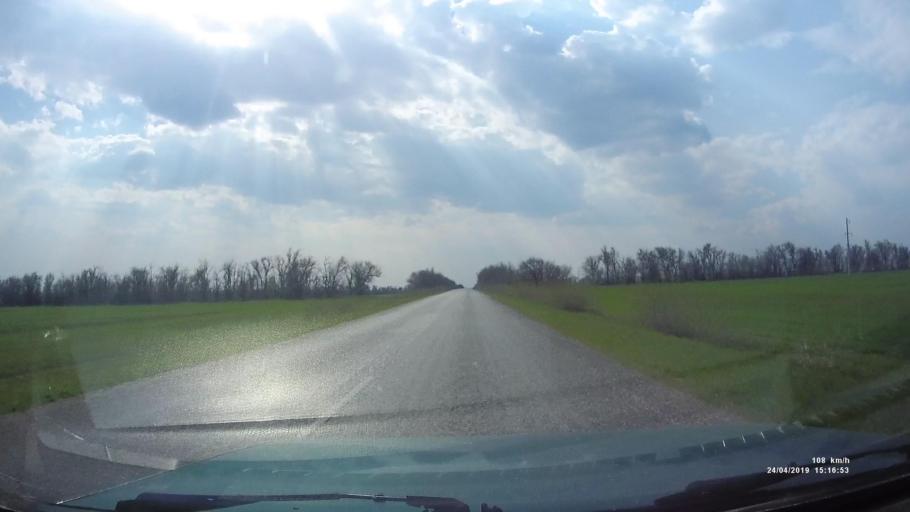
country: RU
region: Rostov
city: Remontnoye
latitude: 46.5465
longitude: 43.2024
